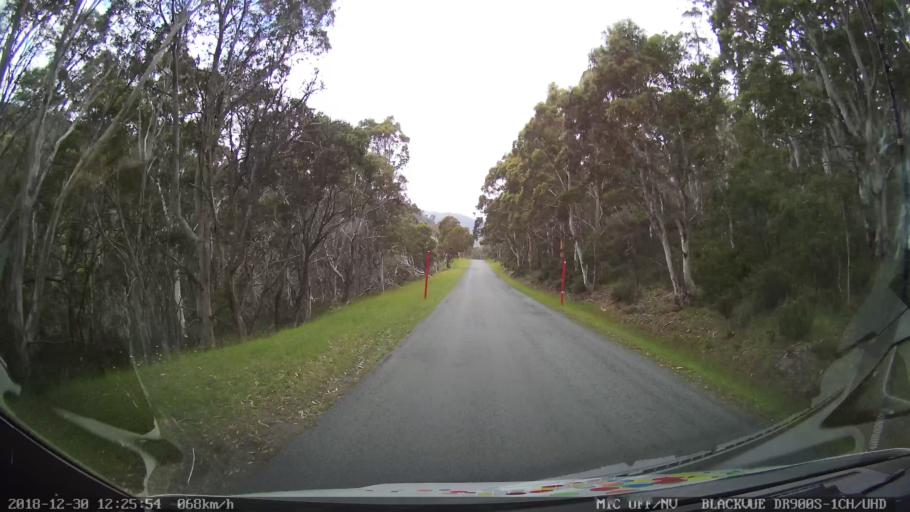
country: AU
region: New South Wales
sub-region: Snowy River
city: Jindabyne
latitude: -36.3451
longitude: 148.4888
